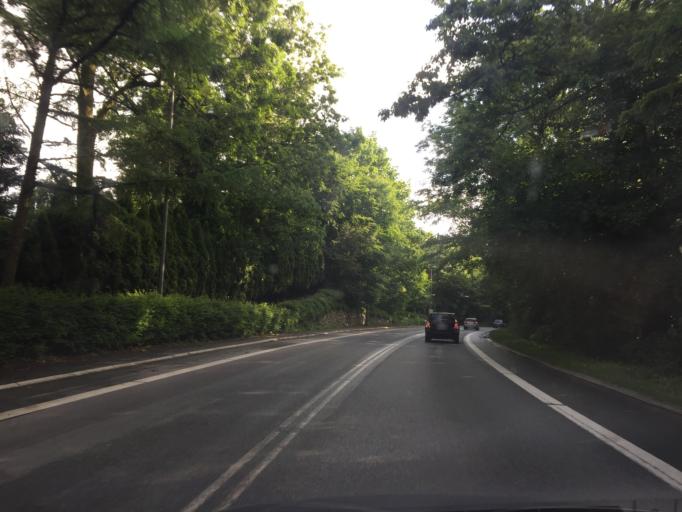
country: DK
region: Zealand
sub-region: Slagelse Kommune
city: Slagelse
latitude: 55.3922
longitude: 11.3665
